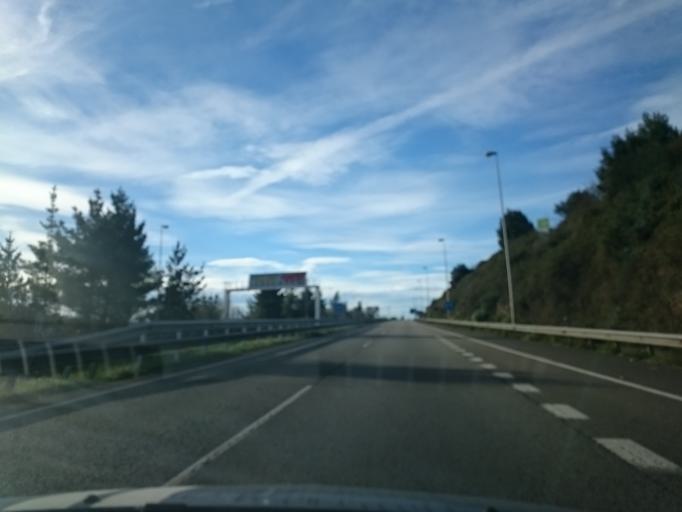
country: ES
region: Asturias
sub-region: Province of Asturias
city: Gijon
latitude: 43.5142
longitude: -5.6643
